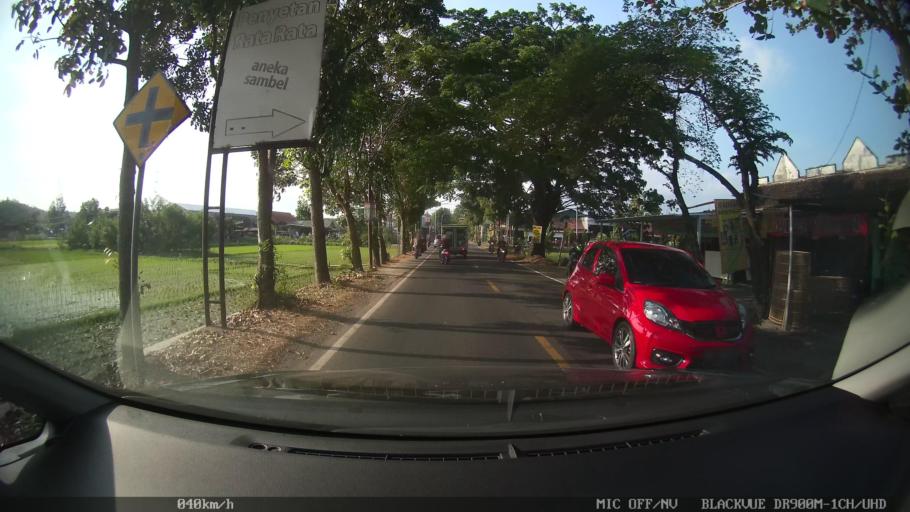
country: ID
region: Daerah Istimewa Yogyakarta
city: Bantul
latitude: -7.8793
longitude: 110.3196
